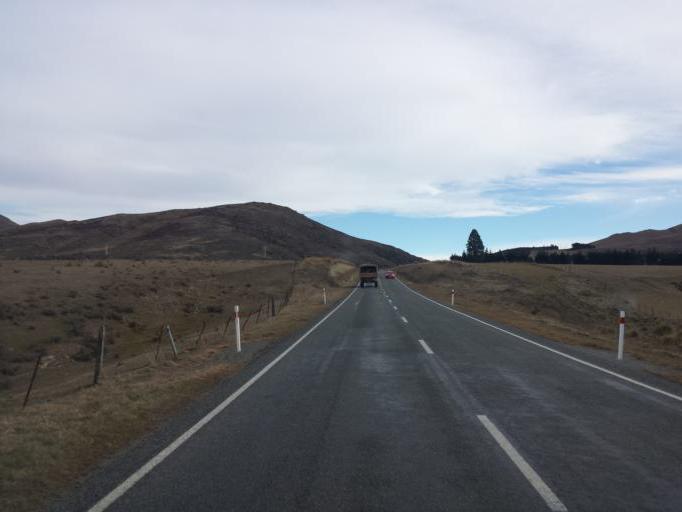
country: NZ
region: Canterbury
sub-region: Timaru District
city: Pleasant Point
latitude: -44.0916
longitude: 170.6281
